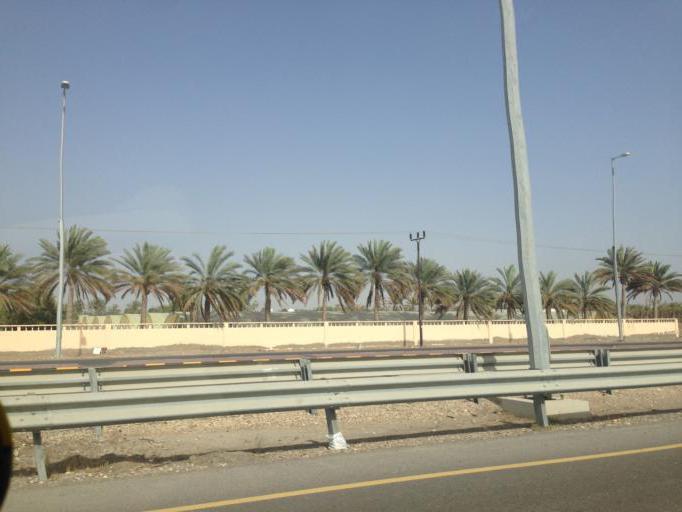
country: OM
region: Al Batinah
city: Barka'
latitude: 23.6497
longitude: 58.0281
